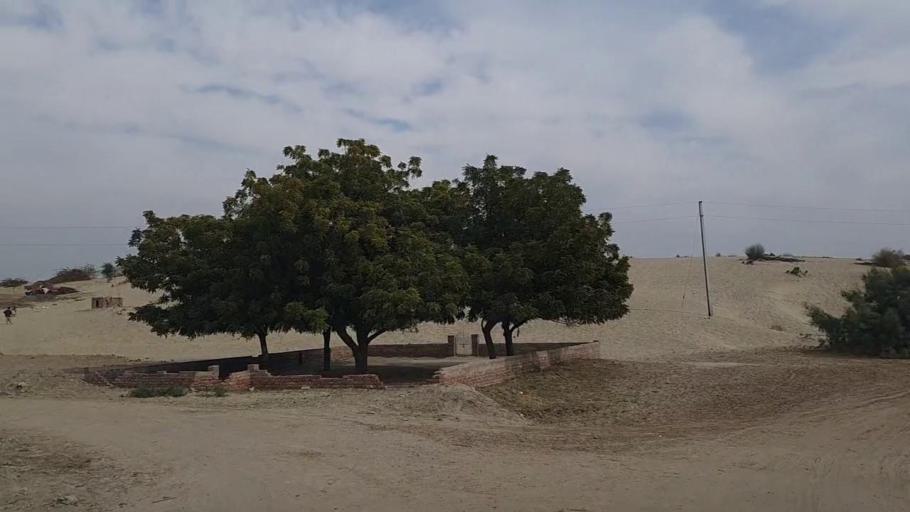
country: PK
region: Sindh
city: Daur
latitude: 26.4288
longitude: 68.4736
